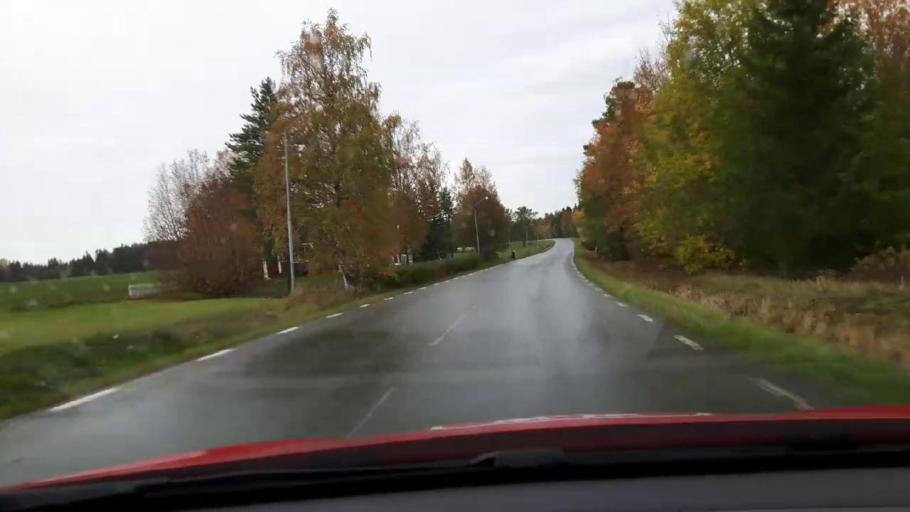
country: SE
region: Jaemtland
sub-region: Bergs Kommun
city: Hoverberg
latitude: 63.0221
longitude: 14.3430
